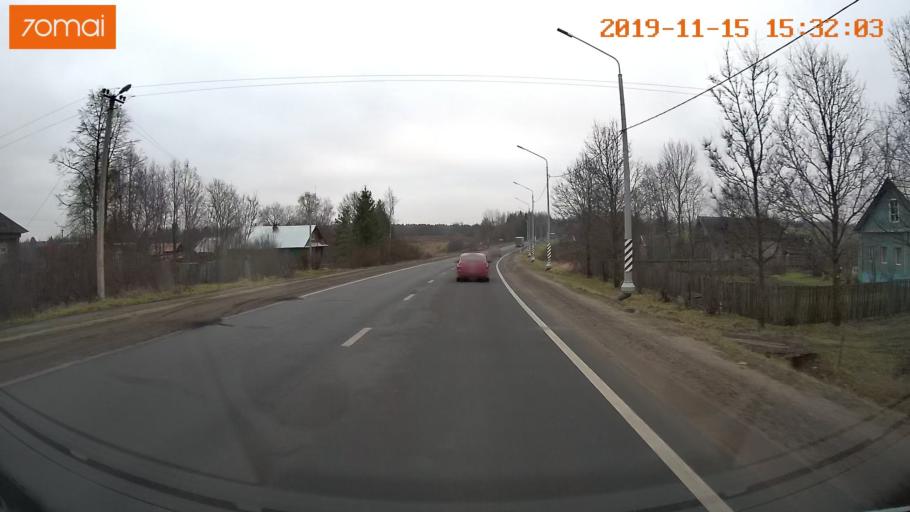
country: RU
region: Jaroslavl
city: Danilov
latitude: 58.0939
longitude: 40.1039
